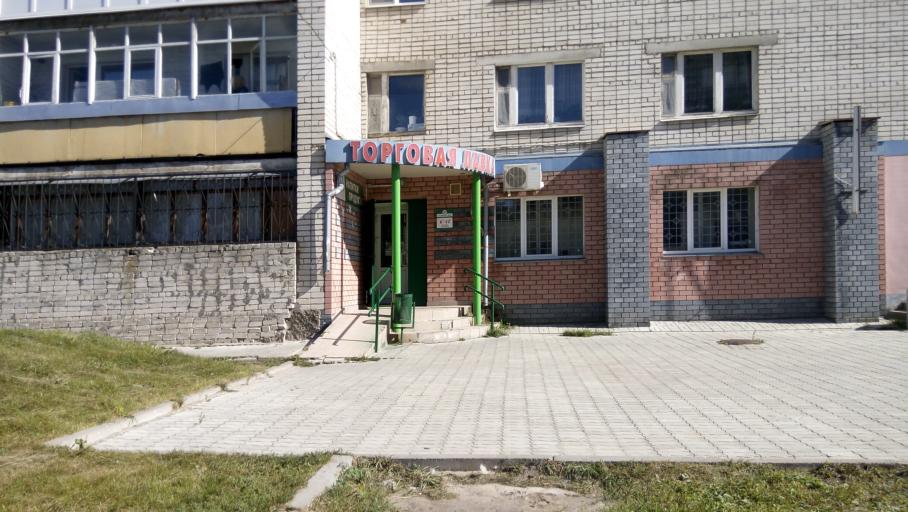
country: RU
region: Nizjnij Novgorod
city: Bor
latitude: 56.3570
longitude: 44.0623
